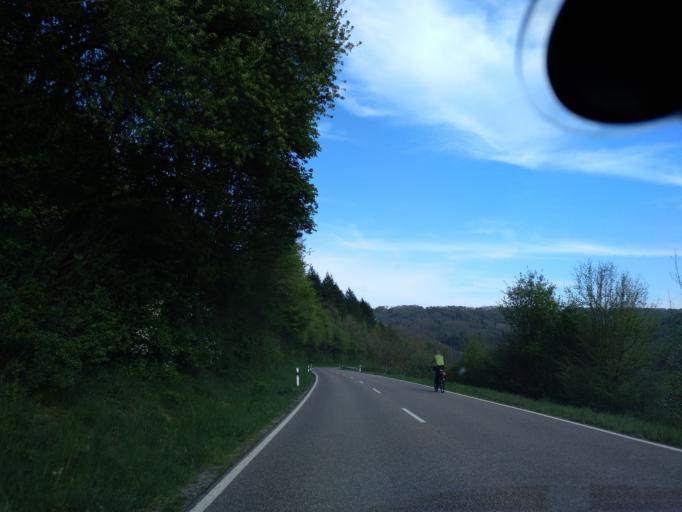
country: DE
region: Baden-Wuerttemberg
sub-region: Regierungsbezirk Stuttgart
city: Braunsbach
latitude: 49.2232
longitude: 9.7565
